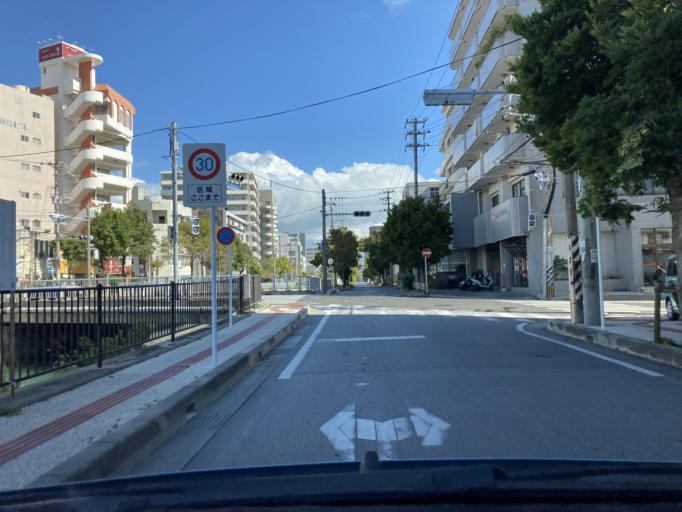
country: JP
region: Okinawa
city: Naha-shi
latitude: 26.2225
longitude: 127.6792
